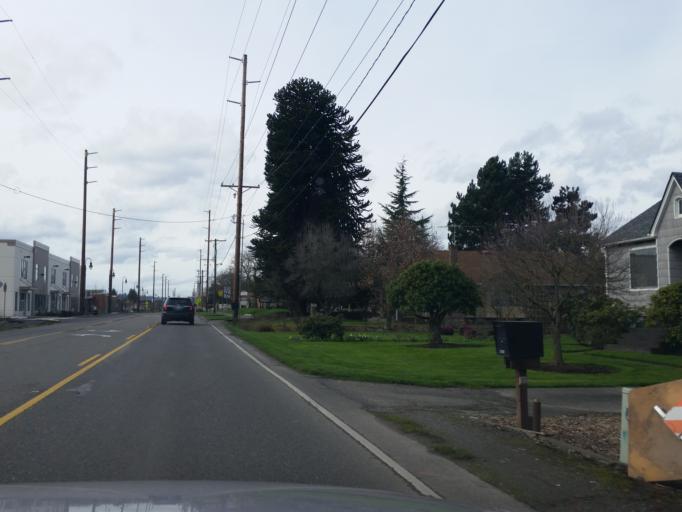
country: US
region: Washington
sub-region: Pierce County
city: Fife
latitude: 47.2391
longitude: -122.3382
